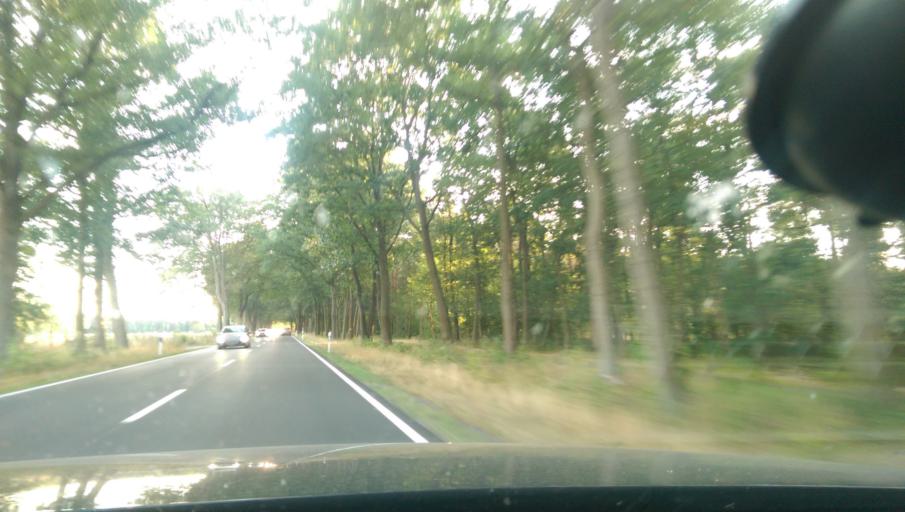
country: DE
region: Lower Saxony
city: Hodenhagen
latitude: 52.7886
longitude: 9.5856
